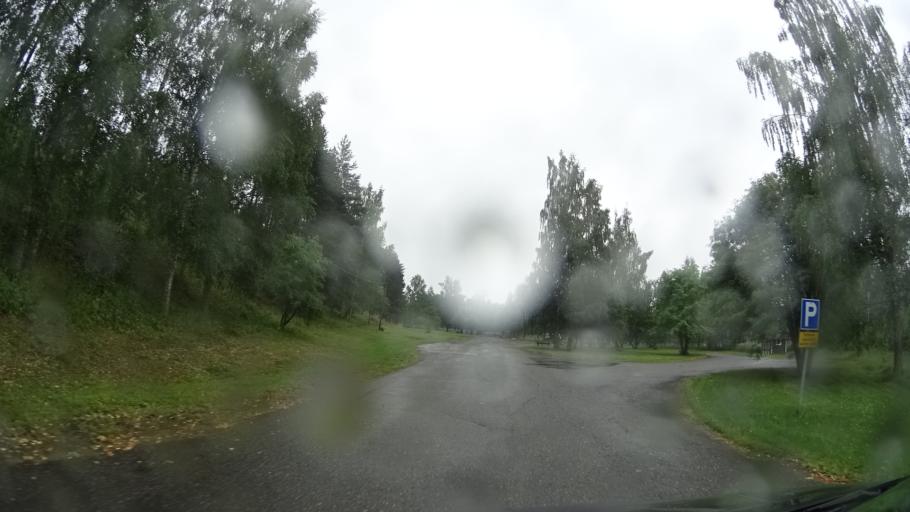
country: FI
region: North Karelia
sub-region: Keski-Karjala
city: Raeaekkylae
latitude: 62.3161
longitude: 29.5122
